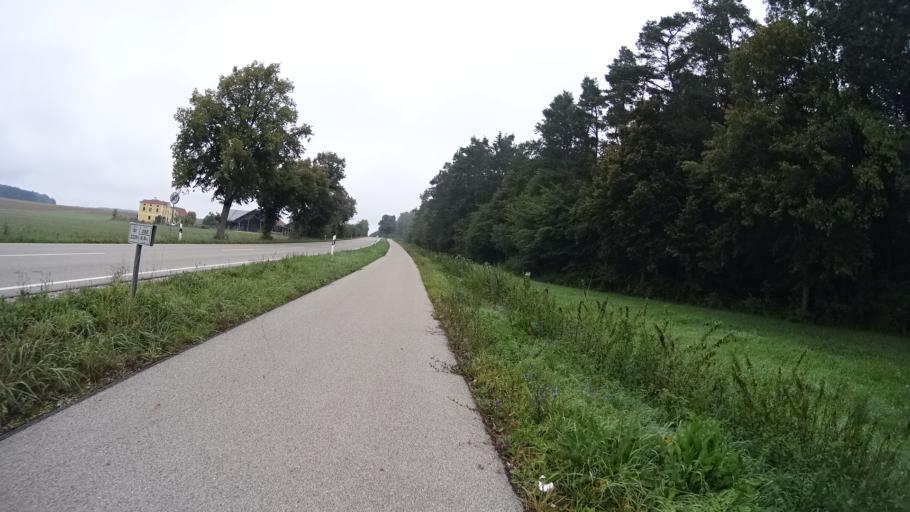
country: DE
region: Bavaria
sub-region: Upper Bavaria
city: Denkendorf
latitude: 48.9130
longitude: 11.4564
